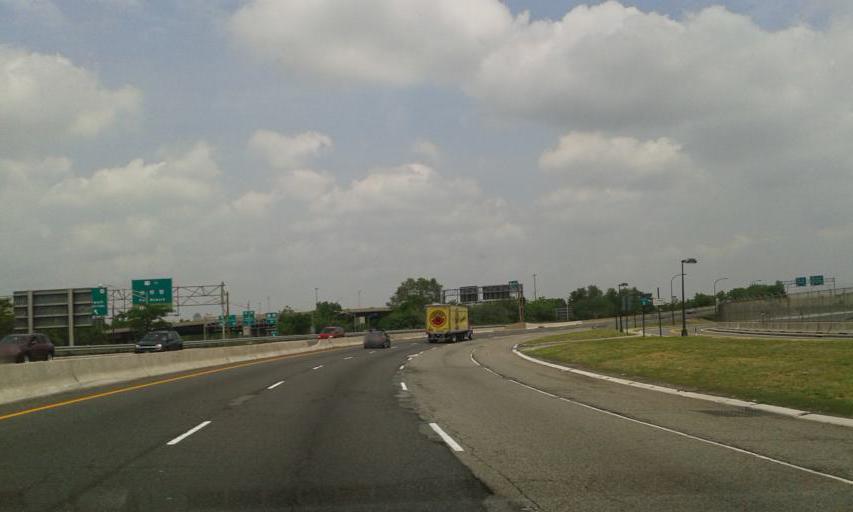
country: US
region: New Jersey
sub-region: Essex County
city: Newark
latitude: 40.7034
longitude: -74.1835
